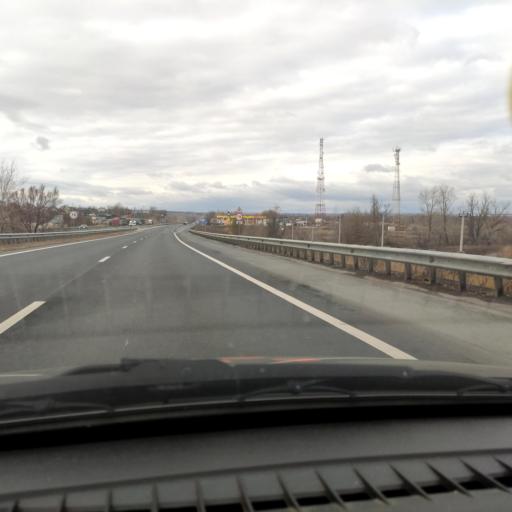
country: RU
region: Samara
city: Novosemeykino
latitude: 53.4200
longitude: 50.3299
